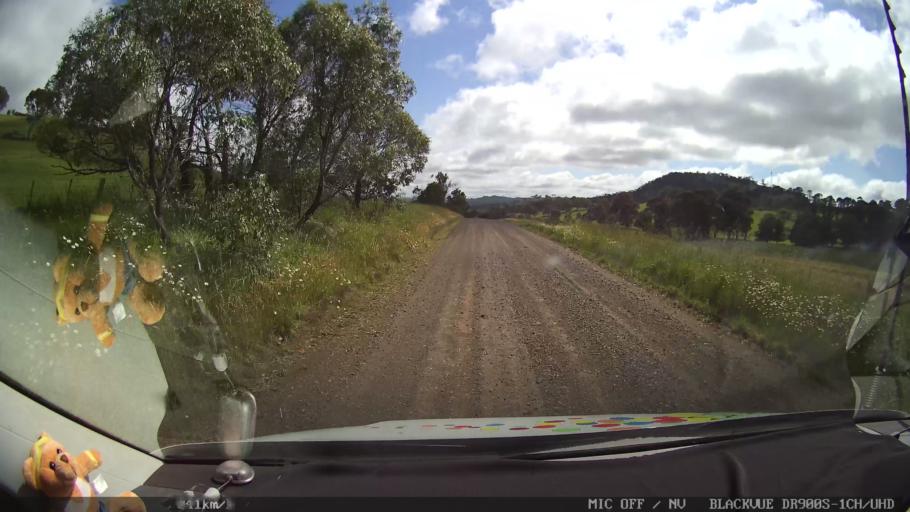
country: AU
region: New South Wales
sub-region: Guyra
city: Guyra
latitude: -30.0073
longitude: 151.6655
